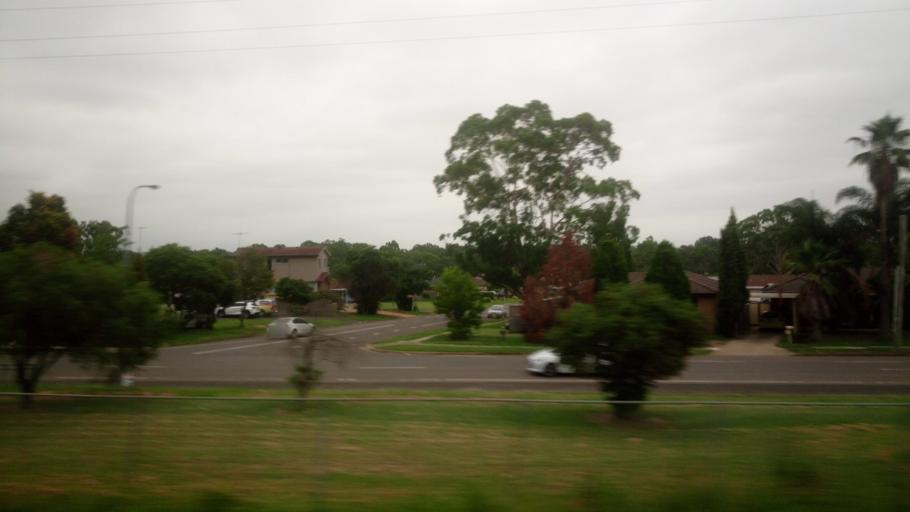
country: AU
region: New South Wales
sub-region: Penrith Municipality
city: Werrington County
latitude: -33.7578
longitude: 150.7427
